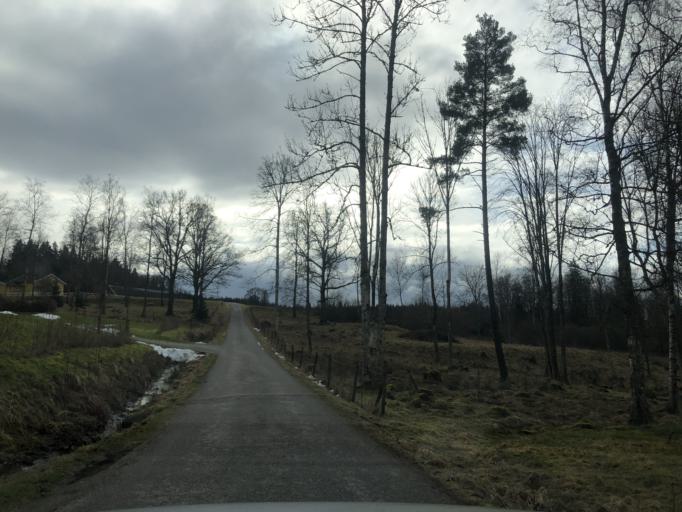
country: SE
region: Vaestra Goetaland
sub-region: Ulricehamns Kommun
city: Ulricehamn
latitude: 57.7669
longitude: 13.4171
